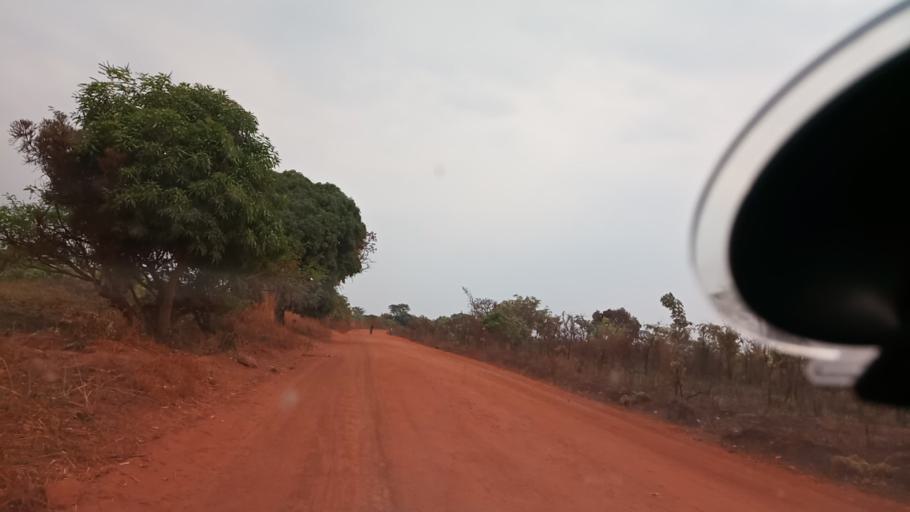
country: ZM
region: Luapula
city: Nchelenge
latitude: -9.1472
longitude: 28.2904
